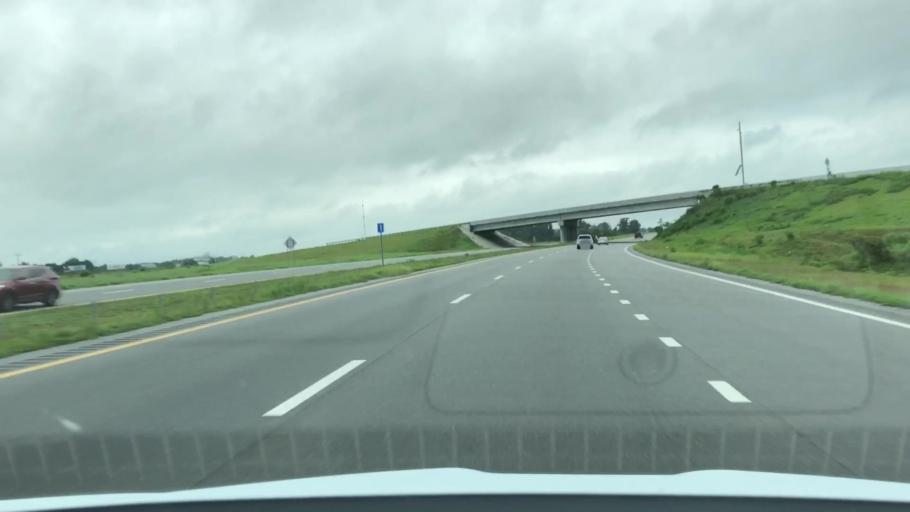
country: US
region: North Carolina
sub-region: Lenoir County
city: La Grange
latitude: 35.3025
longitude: -77.8175
